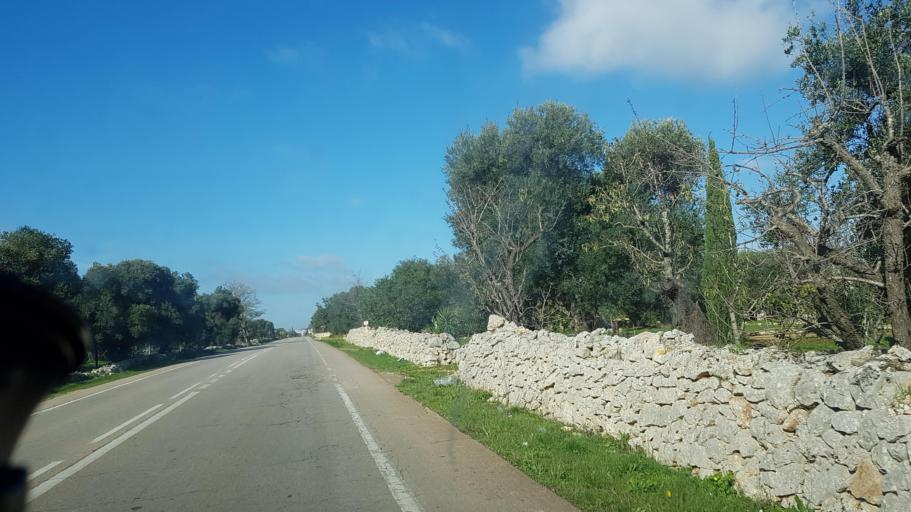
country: IT
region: Apulia
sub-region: Provincia di Brindisi
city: San Vito dei Normanni
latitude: 40.6738
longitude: 17.6908
